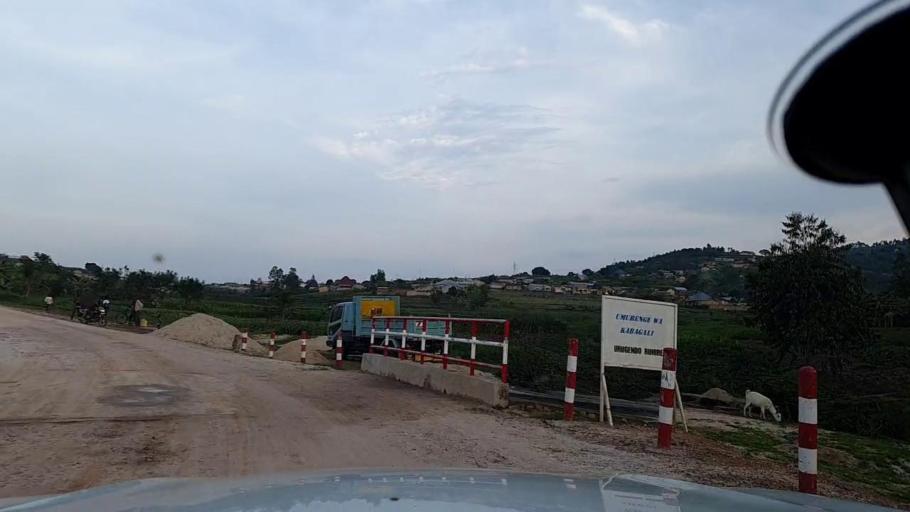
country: RW
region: Southern Province
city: Nyanza
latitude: -2.2268
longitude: 29.6557
